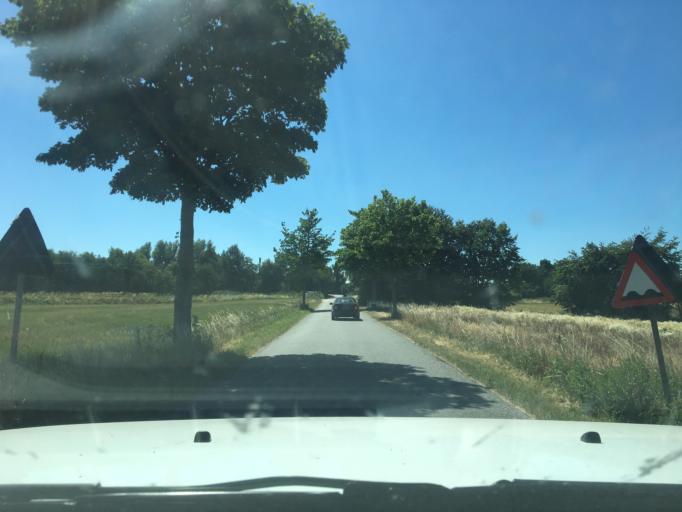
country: DK
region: Central Jutland
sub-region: Syddjurs Kommune
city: Hornslet
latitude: 56.3433
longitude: 10.3857
